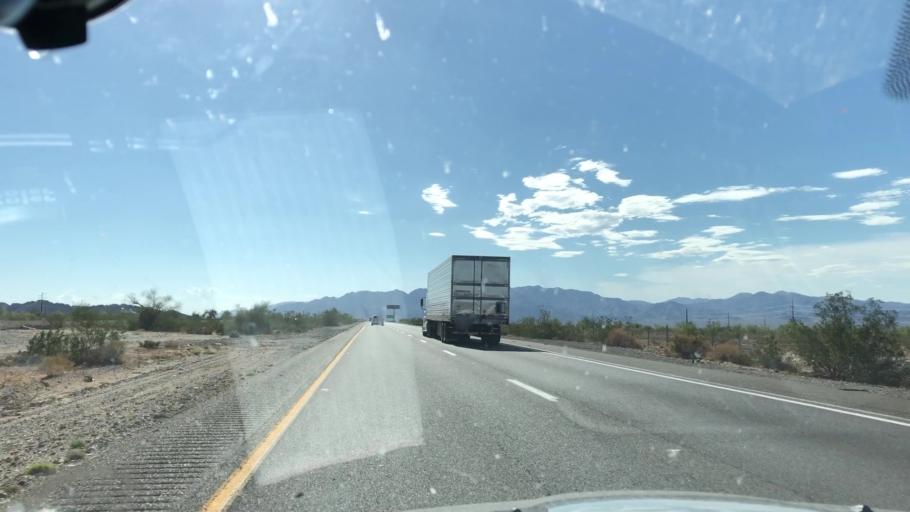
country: US
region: California
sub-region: Imperial County
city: Niland
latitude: 33.7094
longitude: -115.3676
